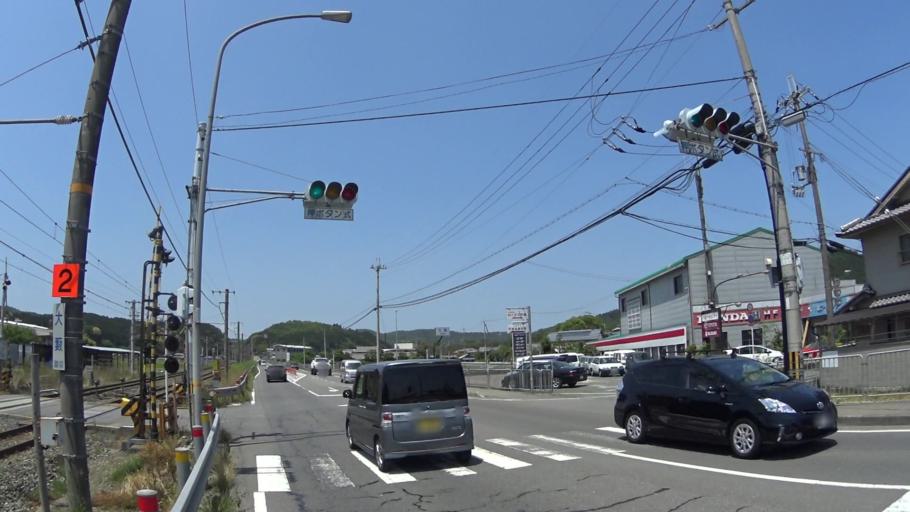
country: JP
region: Kyoto
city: Kameoka
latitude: 35.0756
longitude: 135.5229
